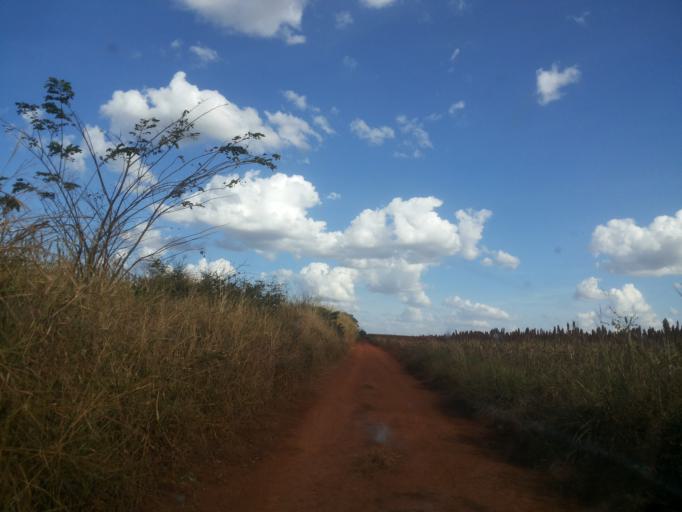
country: BR
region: Minas Gerais
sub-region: Capinopolis
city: Capinopolis
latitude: -18.5975
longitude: -49.4952
